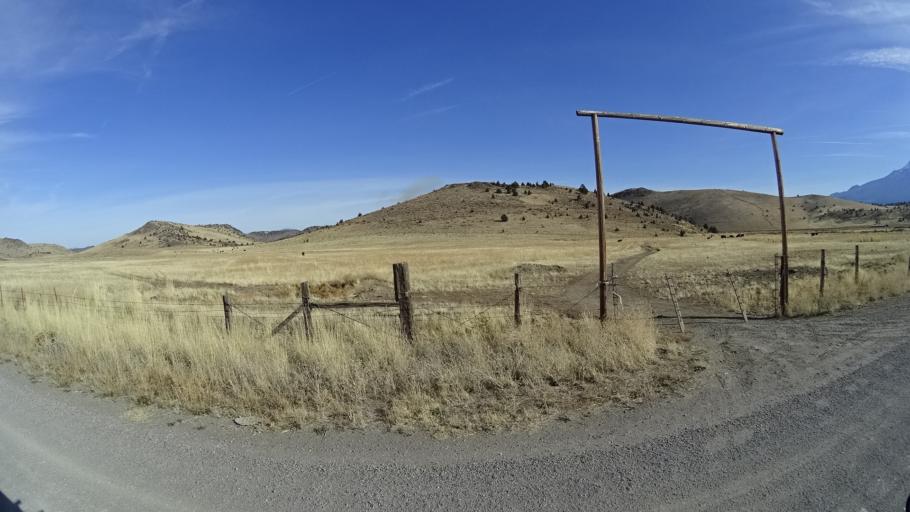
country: US
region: California
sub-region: Siskiyou County
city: Weed
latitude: 41.5050
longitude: -122.4575
